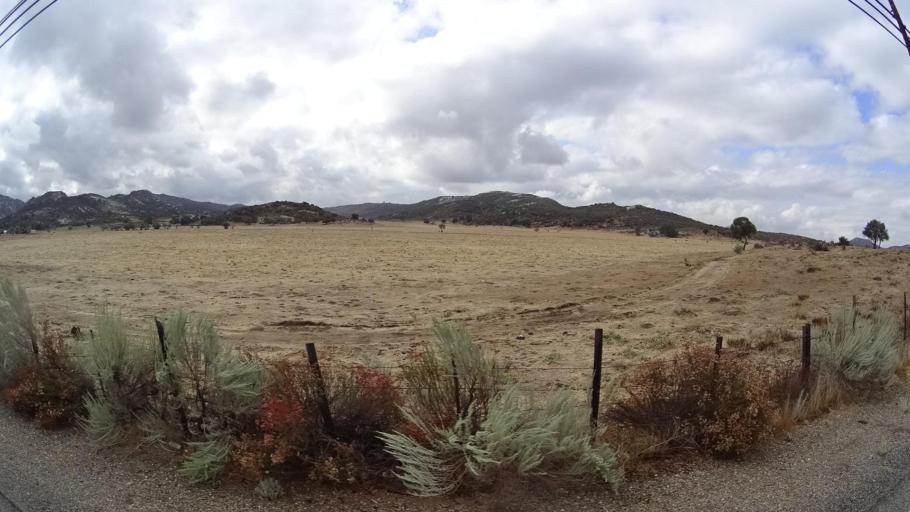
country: US
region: California
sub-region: San Diego County
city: Campo
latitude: 32.6301
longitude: -116.4490
